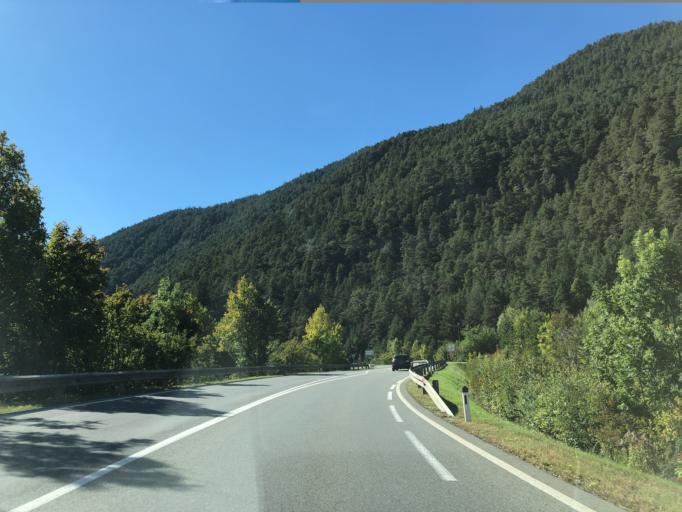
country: AT
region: Tyrol
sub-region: Politischer Bezirk Imst
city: Nassereith
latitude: 47.3031
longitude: 10.8384
